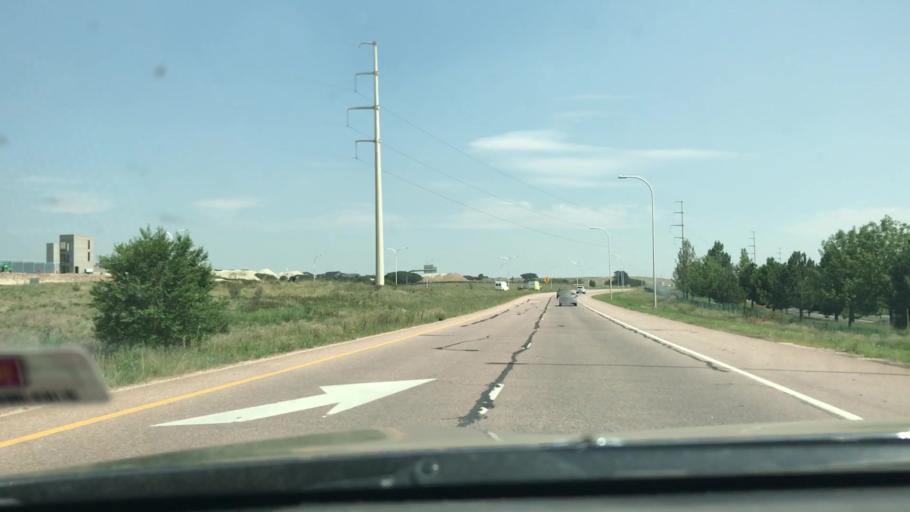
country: US
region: Colorado
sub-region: El Paso County
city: Black Forest
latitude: 38.9825
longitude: -104.7633
